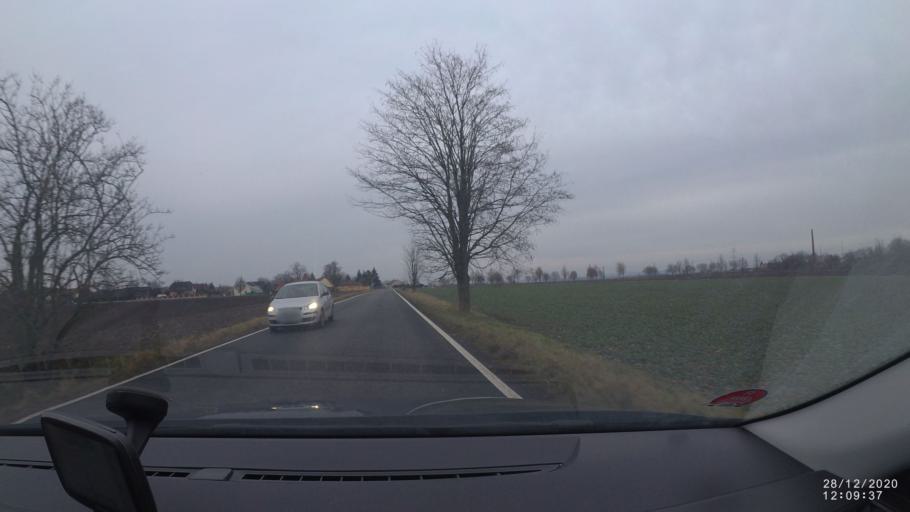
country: CZ
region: Central Bohemia
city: Brandys nad Labem-Stara Boleslav
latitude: 50.1664
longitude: 14.6373
